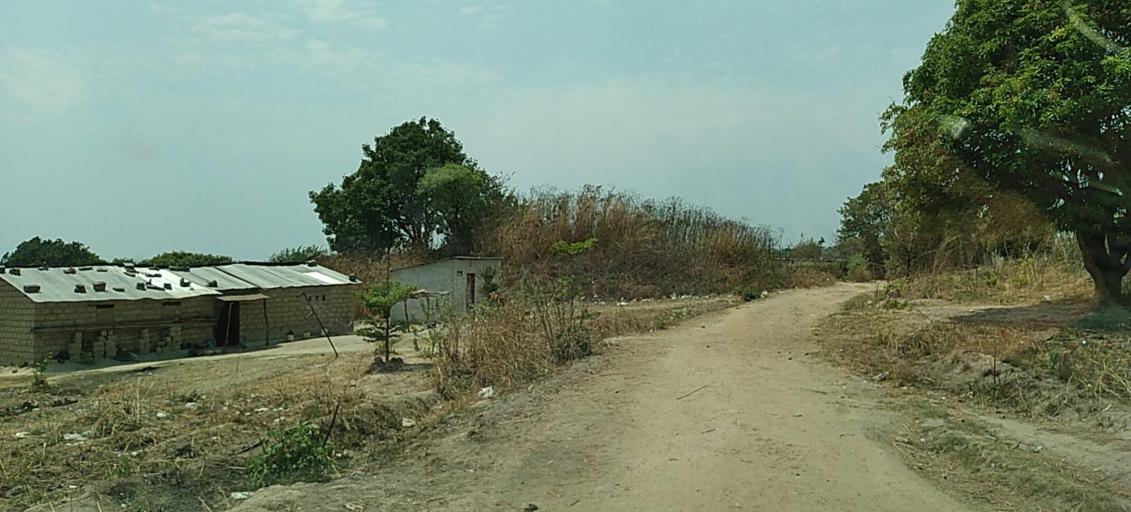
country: ZM
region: Copperbelt
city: Kalulushi
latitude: -12.9565
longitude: 28.1464
